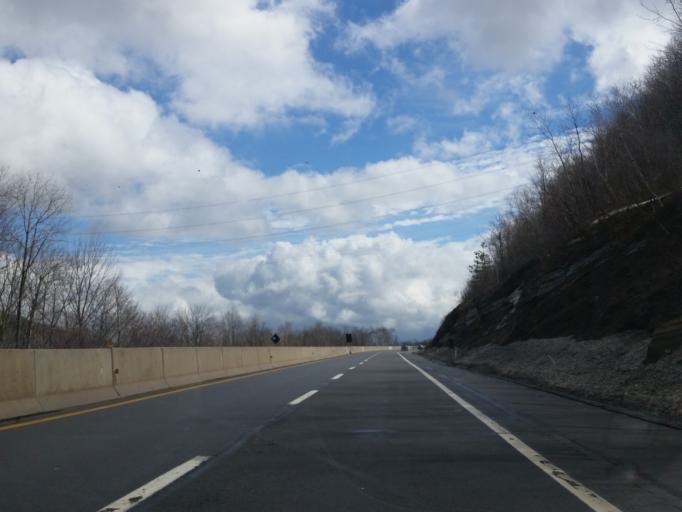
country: US
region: Pennsylvania
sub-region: Lackawanna County
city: Chinchilla
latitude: 41.4606
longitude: -75.6894
